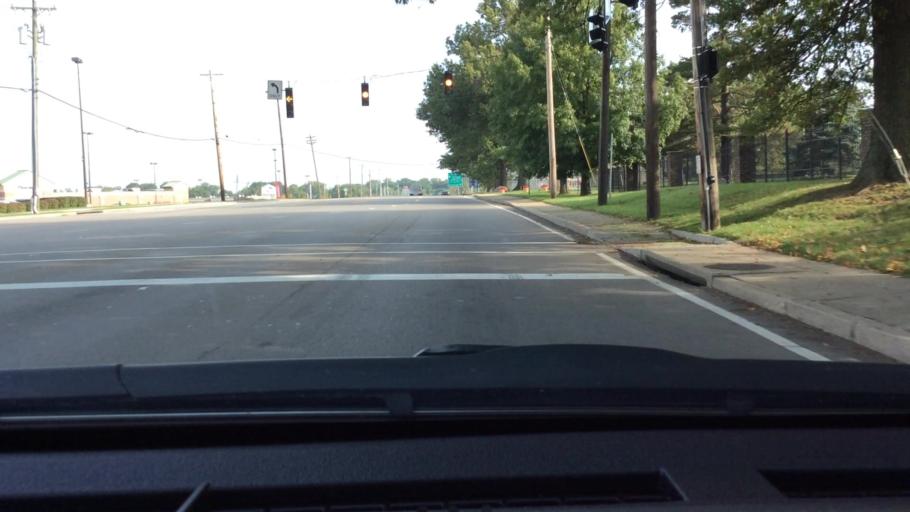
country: US
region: Kentucky
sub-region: Kenton County
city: Fort Mitchell
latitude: 39.0469
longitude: -84.5521
